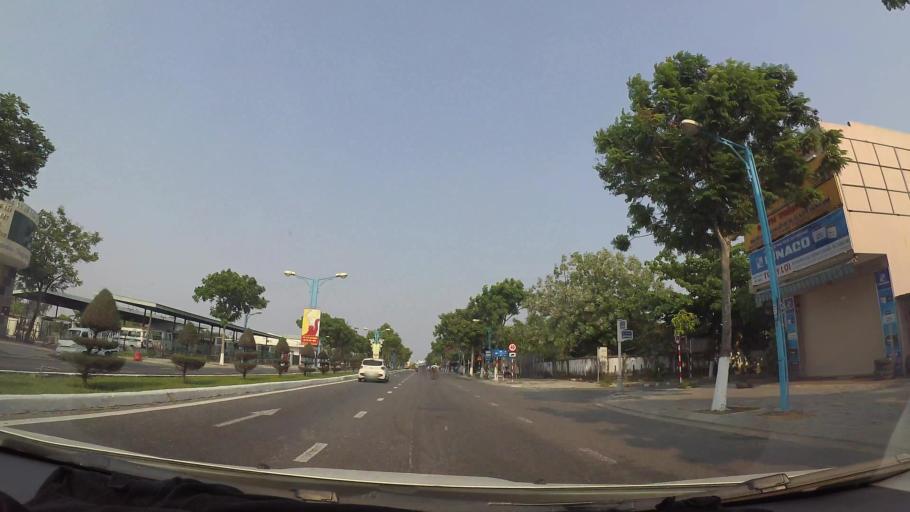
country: VN
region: Da Nang
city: Cam Le
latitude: 16.0231
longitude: 108.2038
